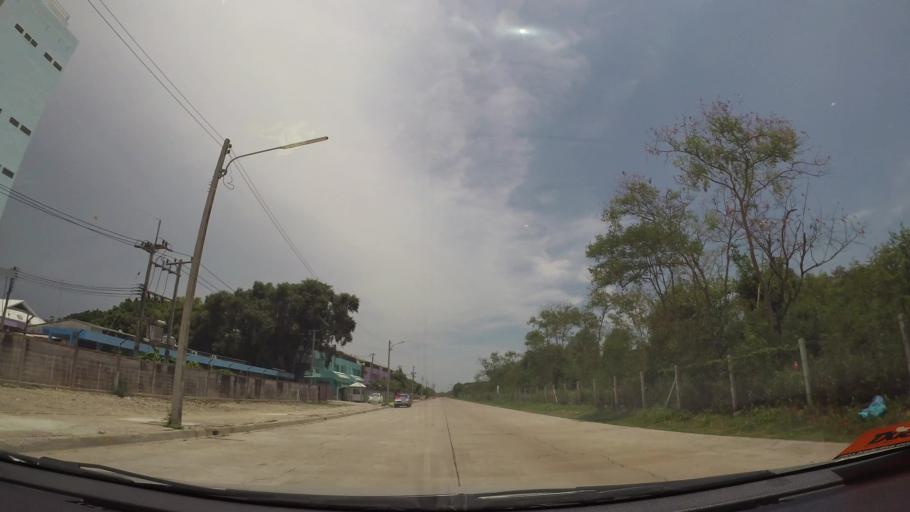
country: TH
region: Chon Buri
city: Chon Buri
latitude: 13.3455
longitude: 100.9530
